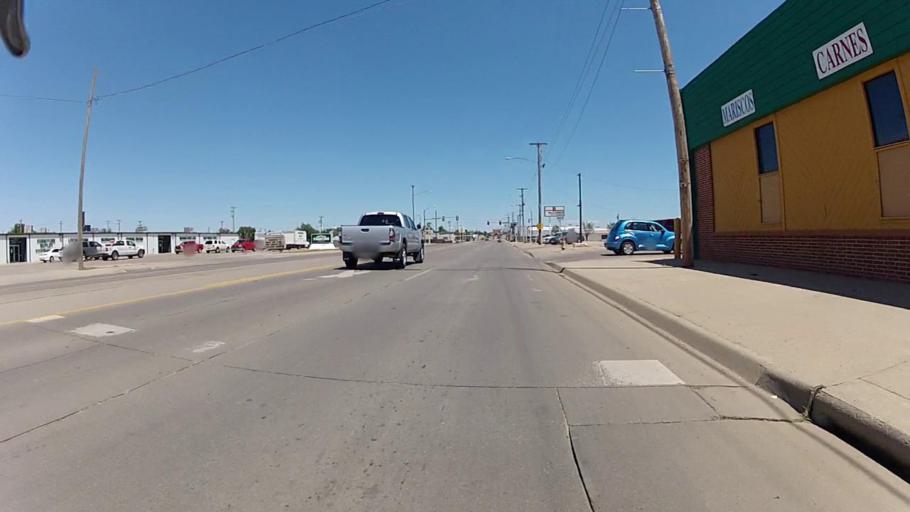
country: US
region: Kansas
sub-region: Ford County
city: Dodge City
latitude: 37.7410
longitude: -100.0194
